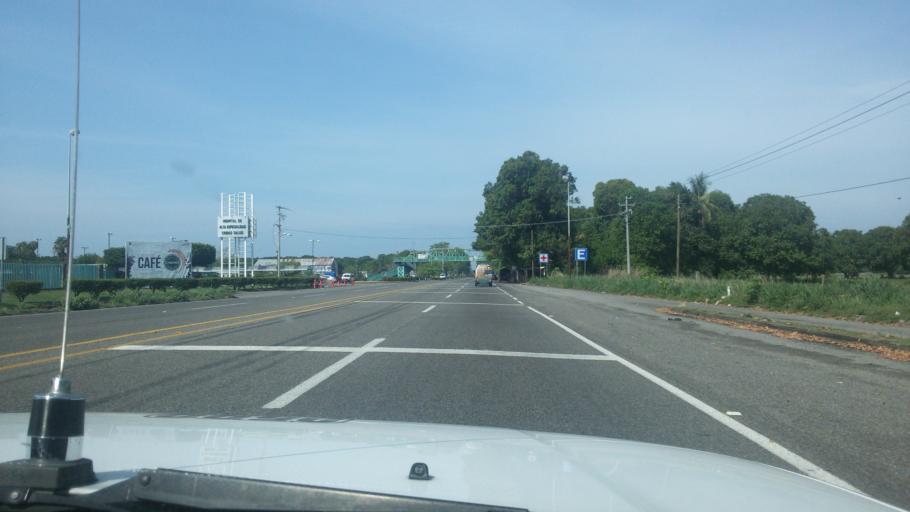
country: MX
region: Chiapas
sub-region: Tapachula
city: Congregacion Reforma
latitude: 14.8114
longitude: -92.3459
